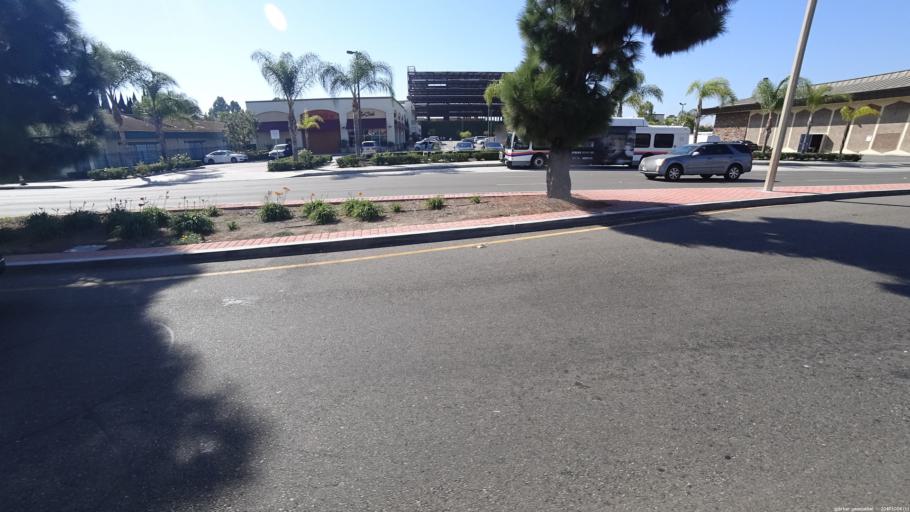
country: US
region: California
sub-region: Orange County
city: Garden Grove
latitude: 33.7733
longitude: -117.9550
